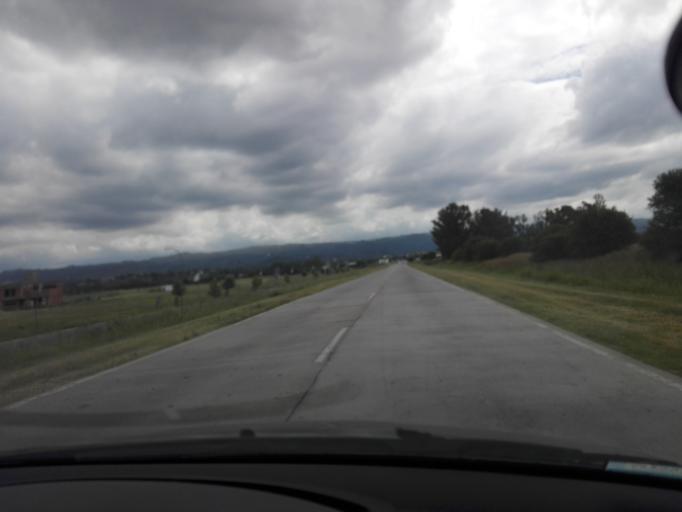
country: AR
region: Cordoba
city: Alta Gracia
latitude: -31.6348
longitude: -64.4201
